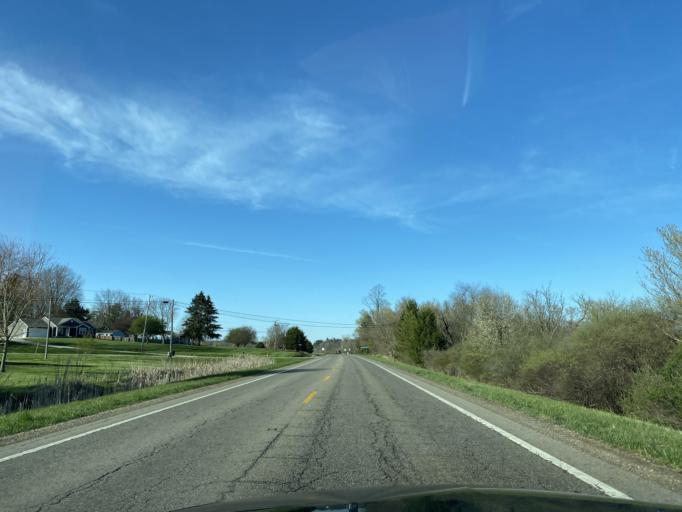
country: US
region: Ohio
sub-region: Wayne County
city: Shreve
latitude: 40.7203
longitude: -82.0005
